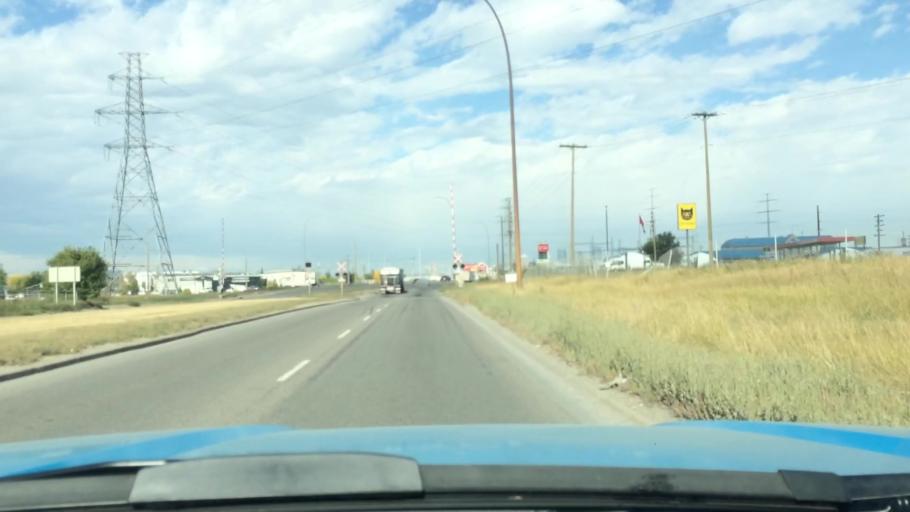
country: CA
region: Alberta
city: Calgary
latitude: 51.0062
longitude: -113.9982
